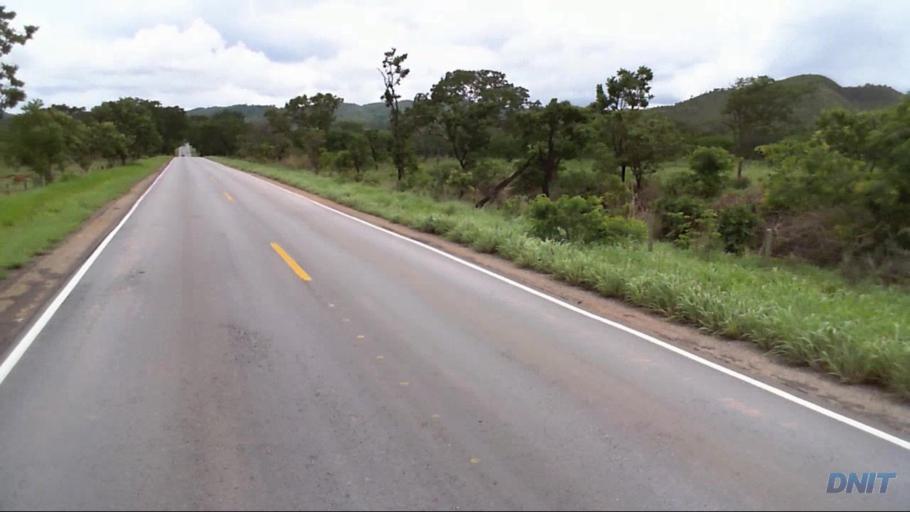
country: BR
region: Goias
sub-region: Padre Bernardo
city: Padre Bernardo
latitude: -15.4504
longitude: -48.2078
